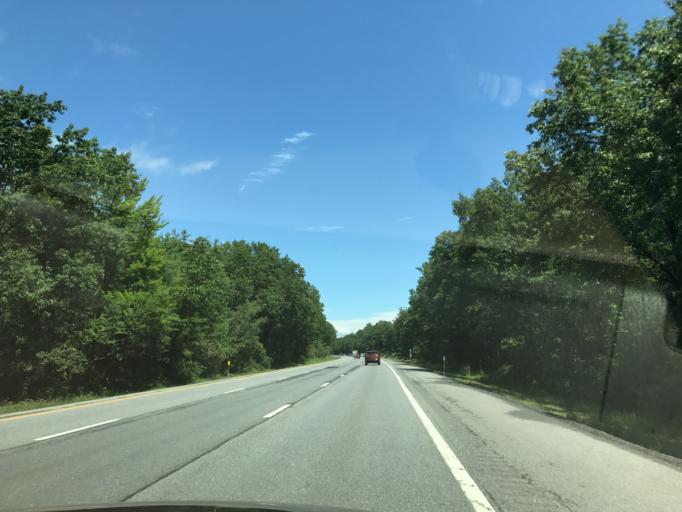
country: US
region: New York
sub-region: Warren County
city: West Glens Falls
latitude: 43.2491
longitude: -73.6855
